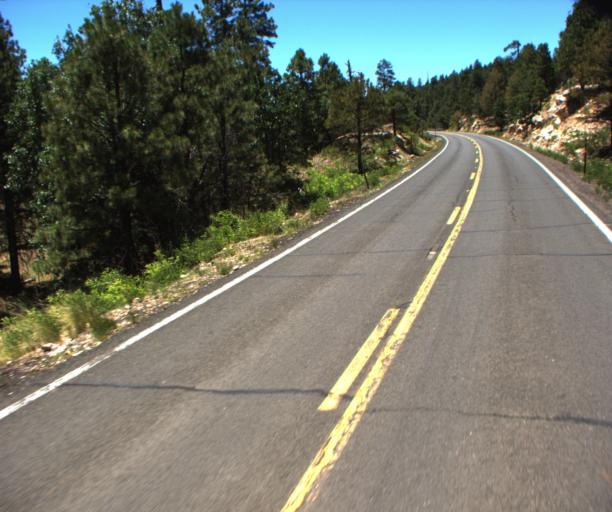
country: US
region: Arizona
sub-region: Gila County
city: Pine
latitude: 34.6042
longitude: -111.2362
